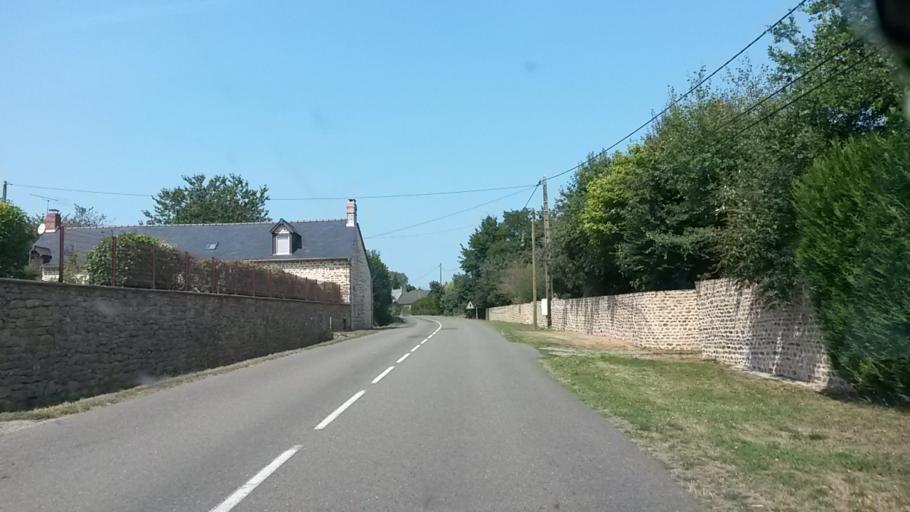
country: FR
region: Pays de la Loire
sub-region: Departement de la Mayenne
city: Saint-Pierre-des-Nids
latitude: 48.3692
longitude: -0.1706
